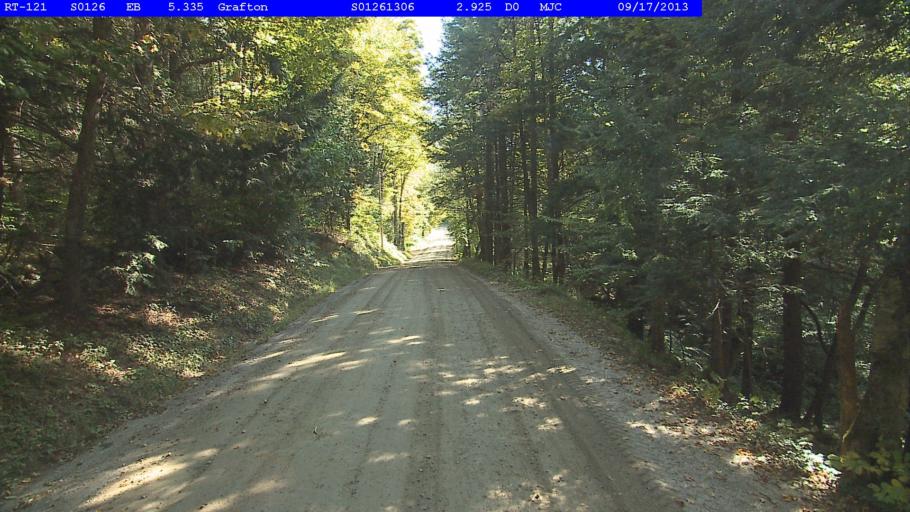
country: US
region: Vermont
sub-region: Windsor County
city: Chester
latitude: 43.1970
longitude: -72.6318
